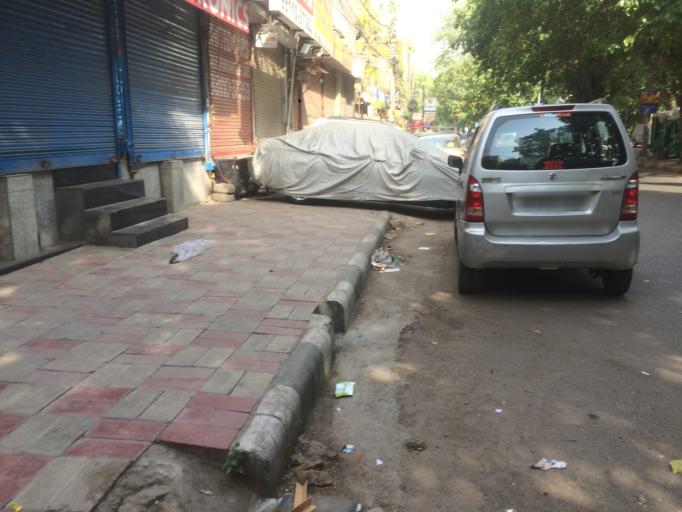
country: IN
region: Uttar Pradesh
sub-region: Gautam Buddha Nagar
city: Noida
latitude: 28.5402
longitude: 77.2509
